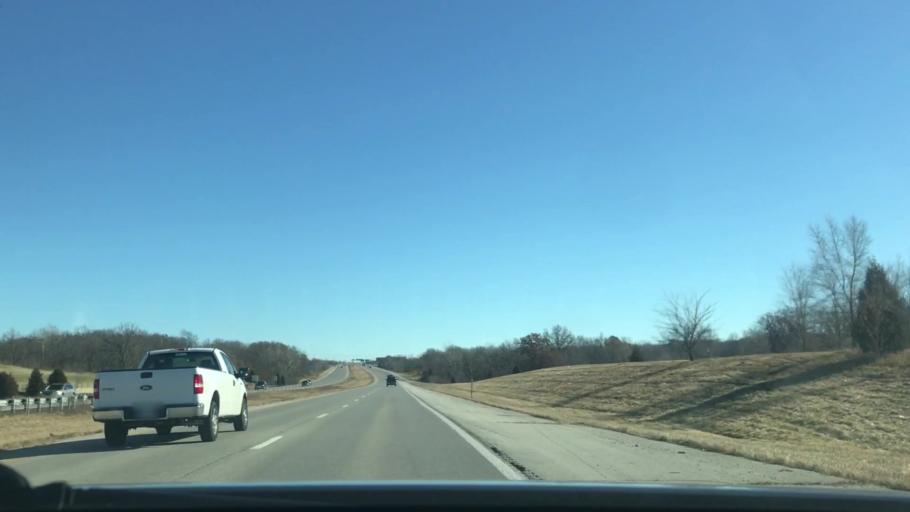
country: US
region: Missouri
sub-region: Platte County
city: Weatherby Lake
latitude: 39.2553
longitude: -94.6826
